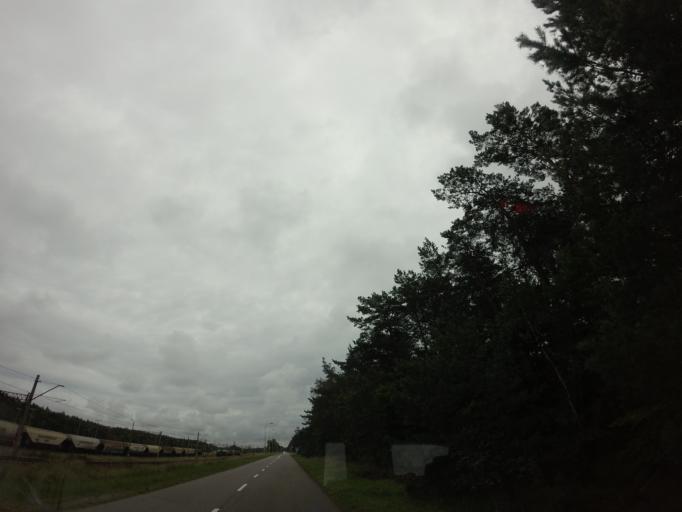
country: PL
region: West Pomeranian Voivodeship
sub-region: Swinoujscie
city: Swinoujscie
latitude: 53.8979
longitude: 14.3243
